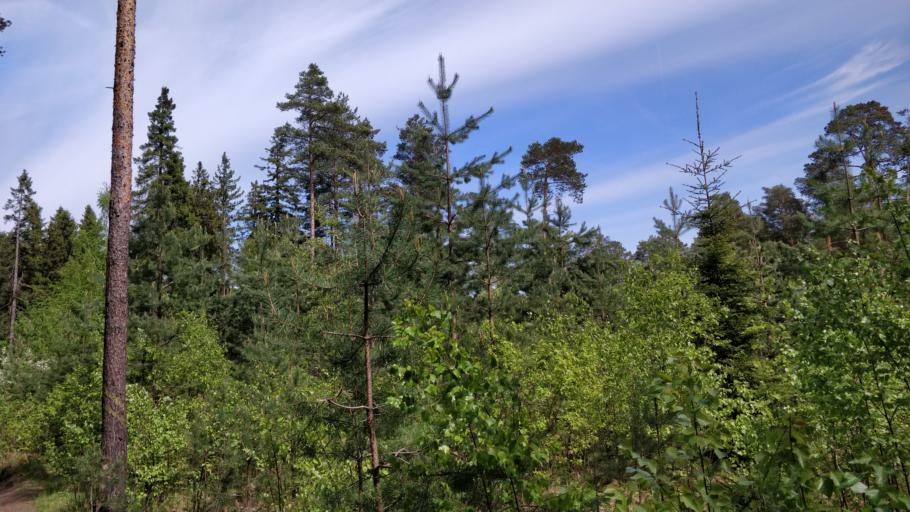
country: RU
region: Perm
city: Kondratovo
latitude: 57.9836
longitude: 56.1374
